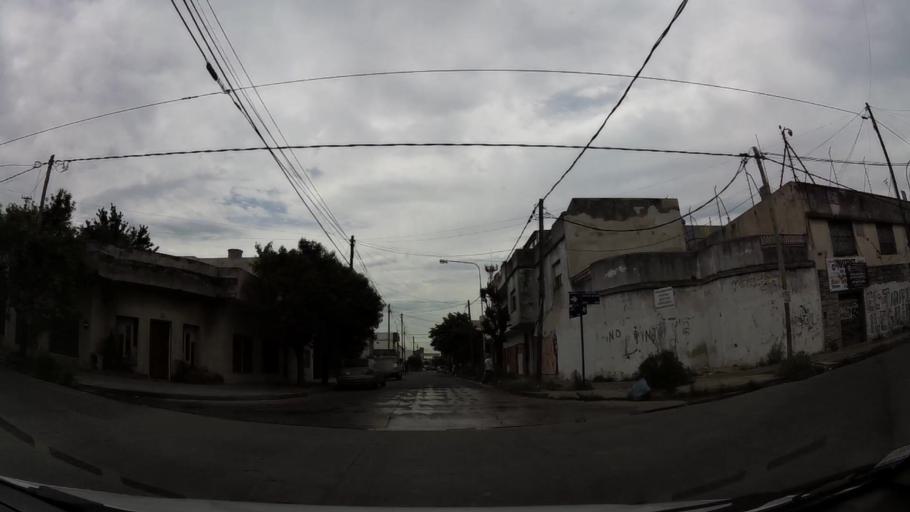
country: AR
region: Buenos Aires F.D.
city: Villa Lugano
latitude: -34.6705
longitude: -58.5111
